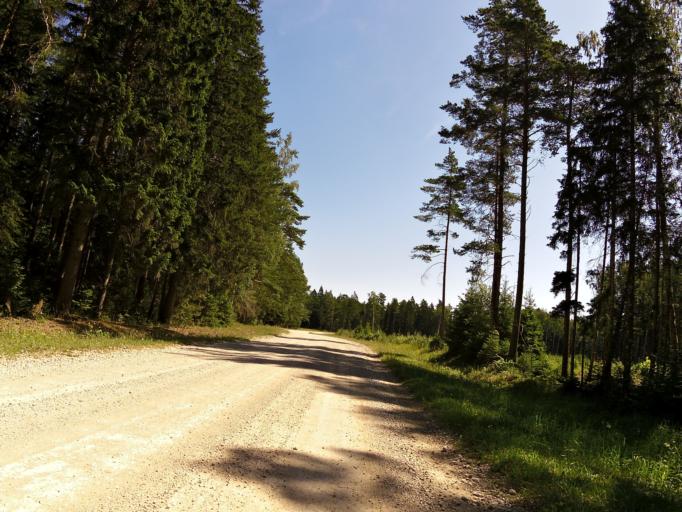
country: EE
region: Hiiumaa
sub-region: Kaerdla linn
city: Kardla
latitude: 58.9205
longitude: 22.3529
